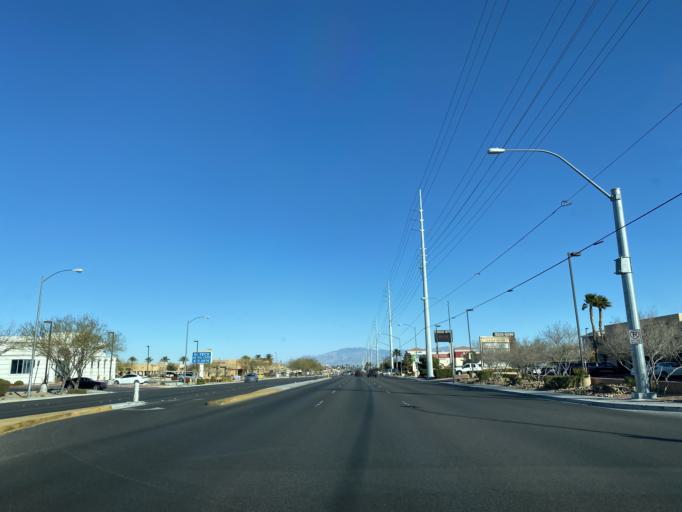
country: US
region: Nevada
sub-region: Clark County
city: Spring Valley
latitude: 36.0742
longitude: -115.2425
